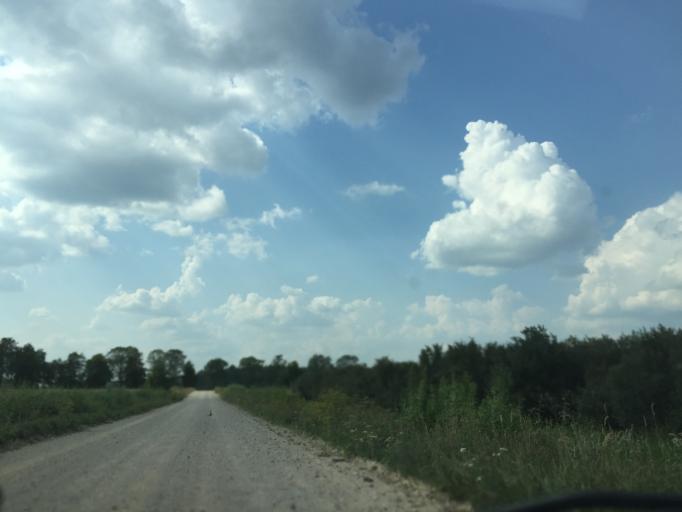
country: LV
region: Auces Novads
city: Auce
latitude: 56.4270
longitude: 22.9635
